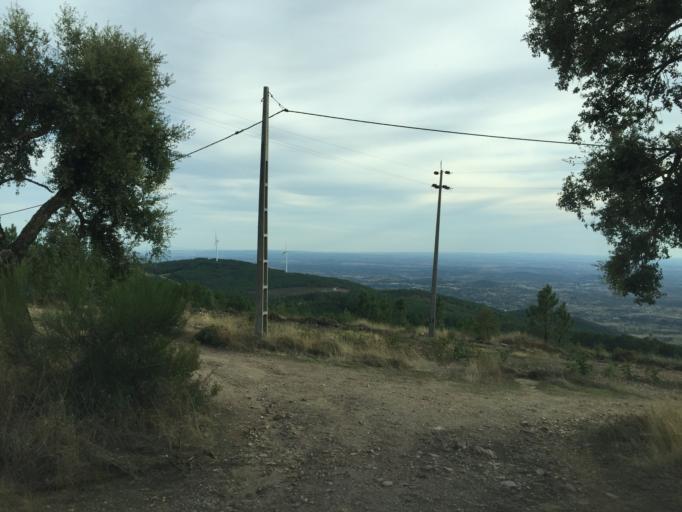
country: PT
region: Portalegre
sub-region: Portalegre
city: Reguengo
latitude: 39.3132
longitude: -7.3602
